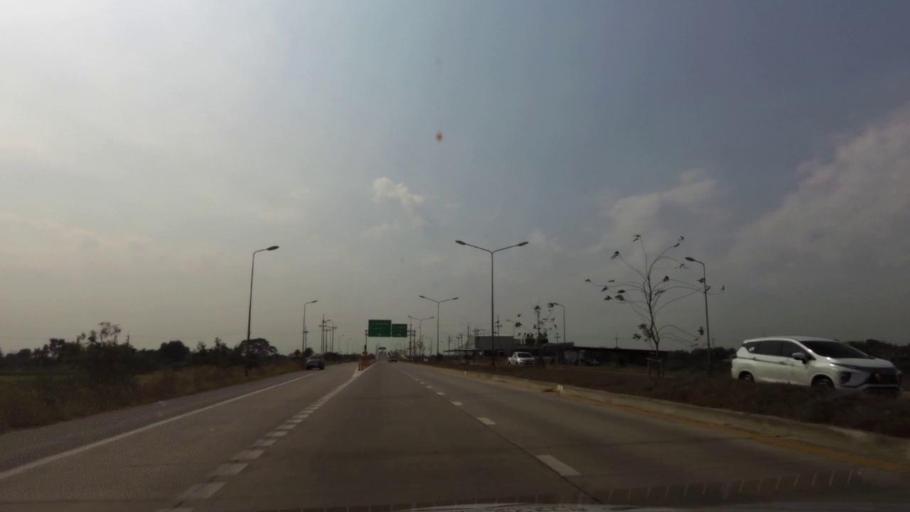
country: TH
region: Phra Nakhon Si Ayutthaya
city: Phra Nakhon Si Ayutthaya
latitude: 14.3312
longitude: 100.5899
